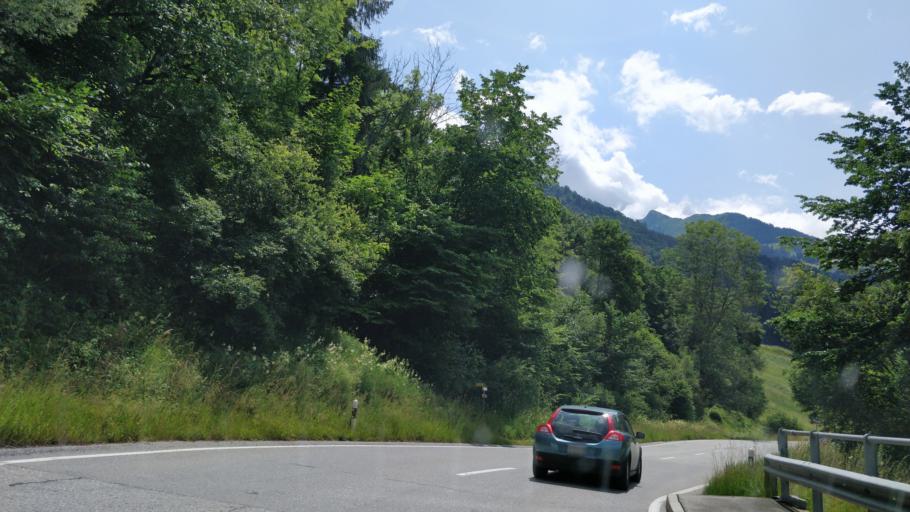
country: CH
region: Grisons
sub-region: Surselva District
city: Ilanz
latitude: 46.7562
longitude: 9.2152
